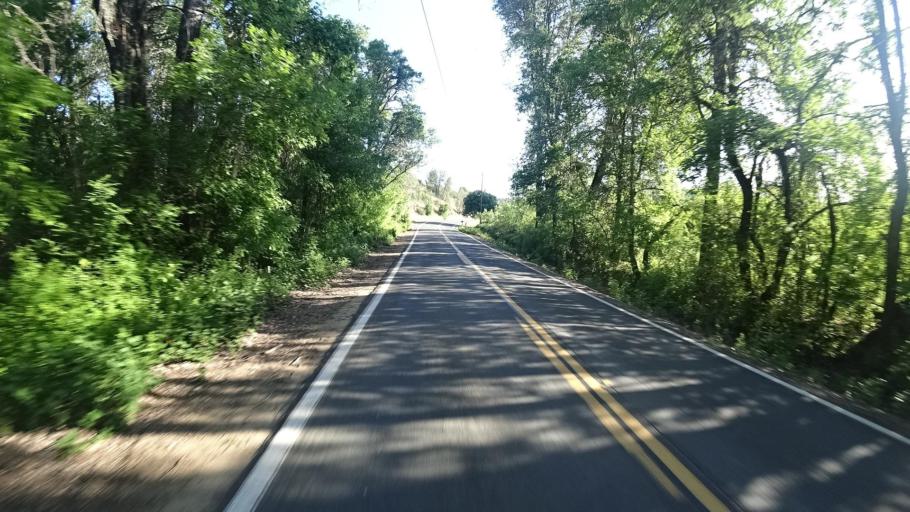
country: US
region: California
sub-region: Lake County
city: North Lakeport
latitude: 39.0881
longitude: -122.9498
